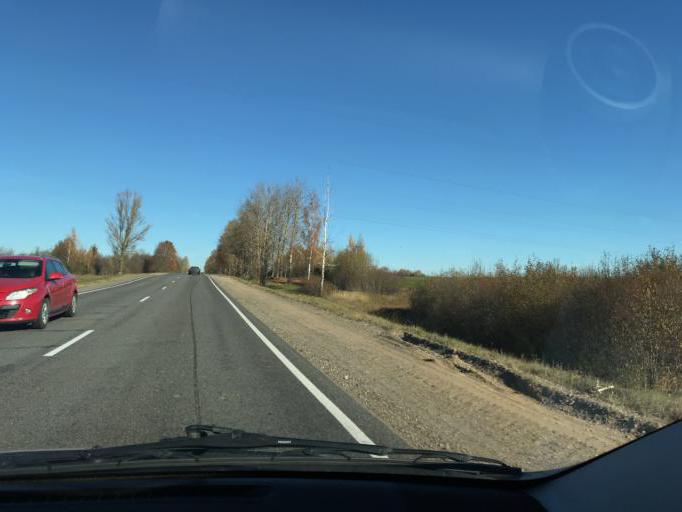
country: BY
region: Vitebsk
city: Lyepyel'
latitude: 55.0124
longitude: 28.7402
